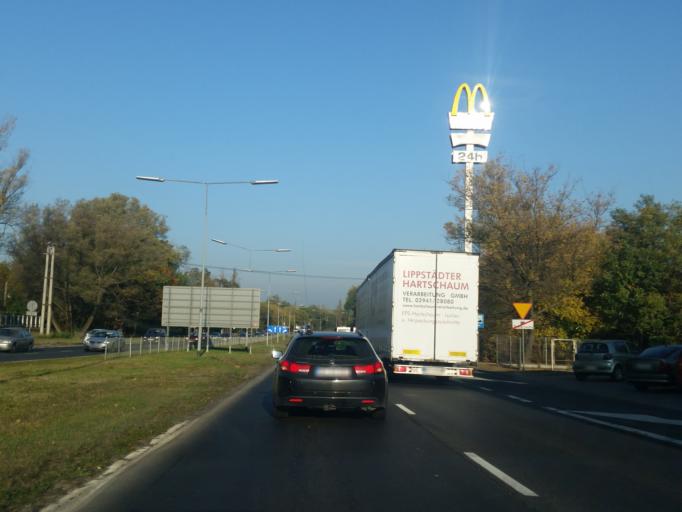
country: PL
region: Masovian Voivodeship
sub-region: Warszawa
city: Bielany
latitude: 52.3078
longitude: 20.9298
